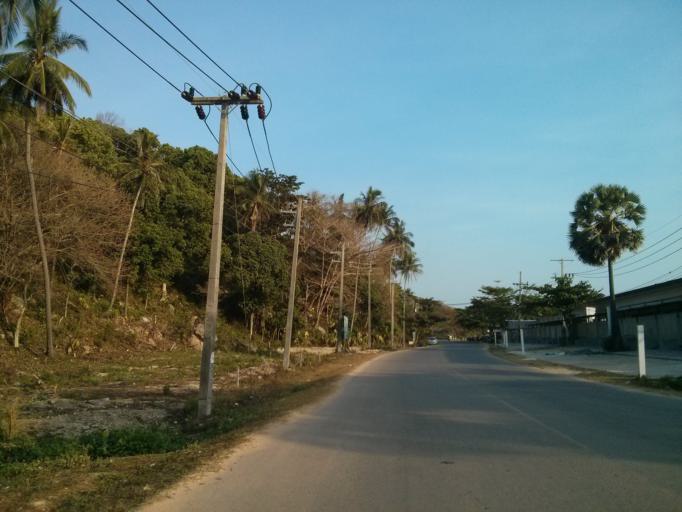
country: TH
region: Krabi
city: Ko Lanta
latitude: 7.5557
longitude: 99.0397
